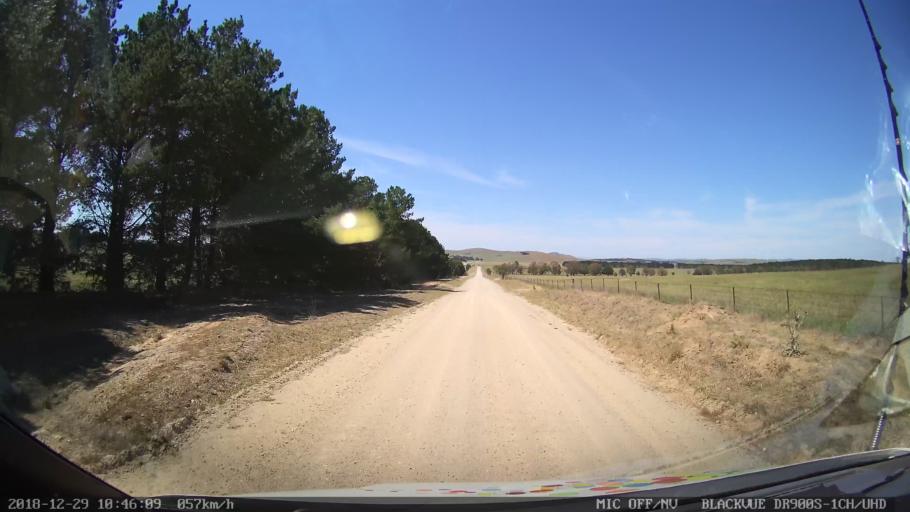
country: AU
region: New South Wales
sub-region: Palerang
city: Bungendore
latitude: -35.0478
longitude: 149.5167
